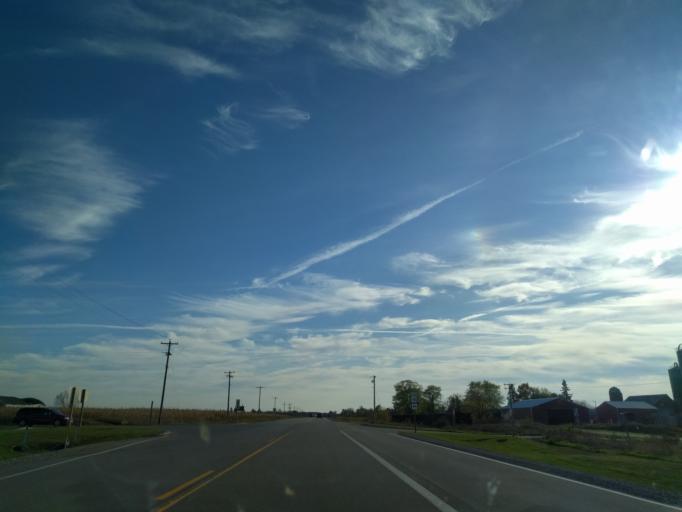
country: US
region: Wisconsin
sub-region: Marinette County
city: Peshtigo
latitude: 45.3674
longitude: -87.9529
